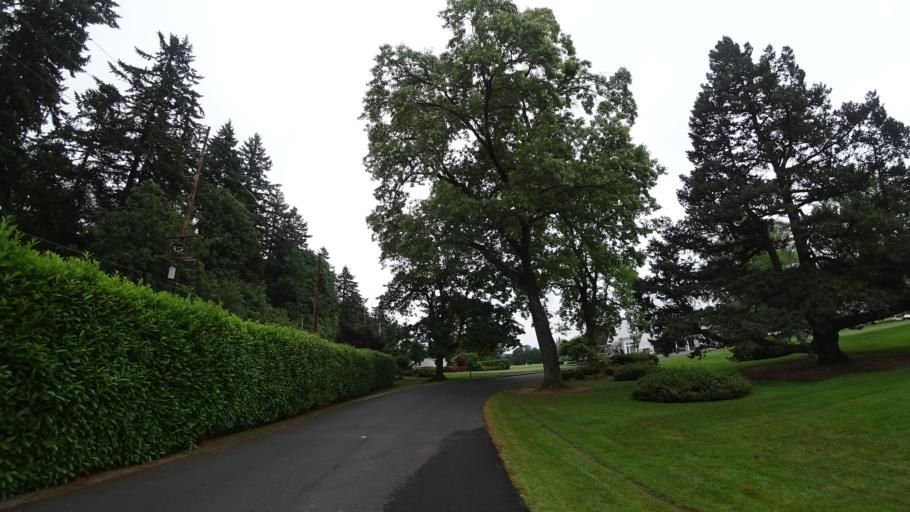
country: US
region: Oregon
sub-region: Clackamas County
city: Milwaukie
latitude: 45.4499
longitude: -122.6517
